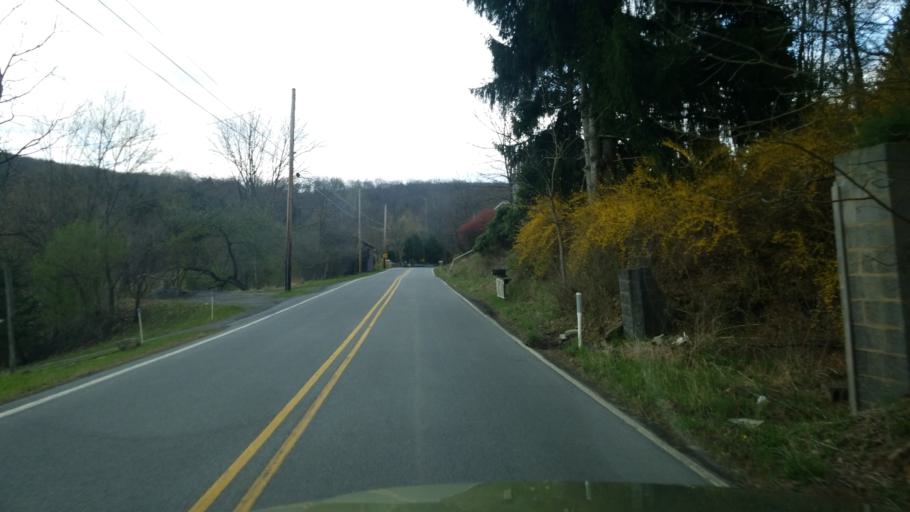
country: US
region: Pennsylvania
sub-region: Clearfield County
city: Curwensville
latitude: 40.8496
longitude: -78.4444
